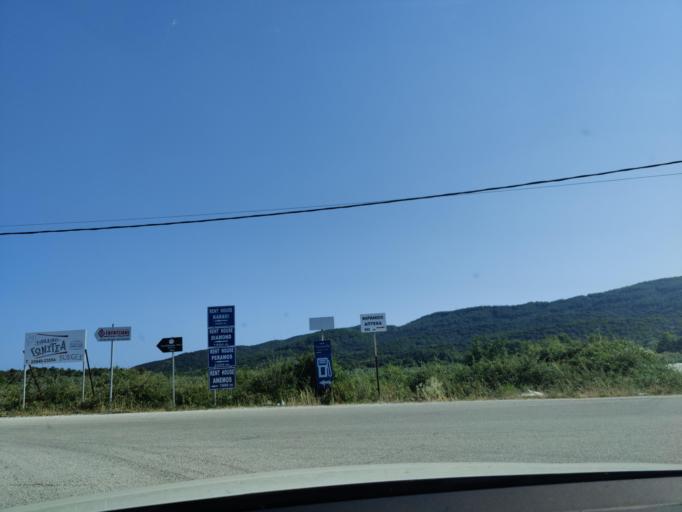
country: GR
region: East Macedonia and Thrace
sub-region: Nomos Kavalas
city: Nea Iraklitsa
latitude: 40.8666
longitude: 24.2941
